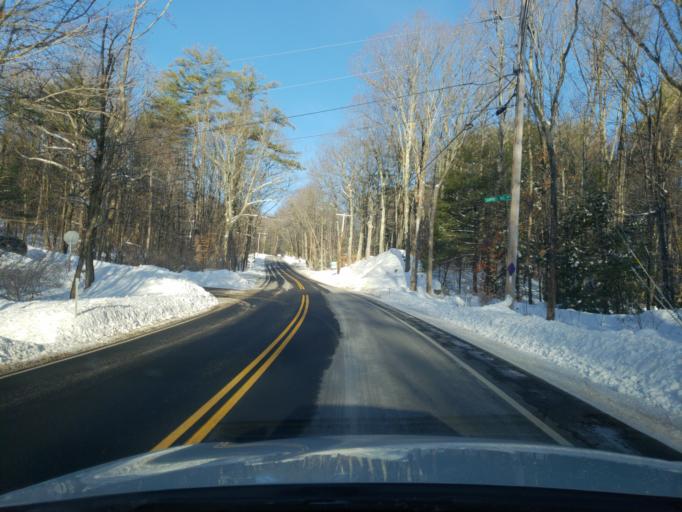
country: US
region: New Hampshire
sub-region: Hillsborough County
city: Greenfield
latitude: 43.0011
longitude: -71.8299
